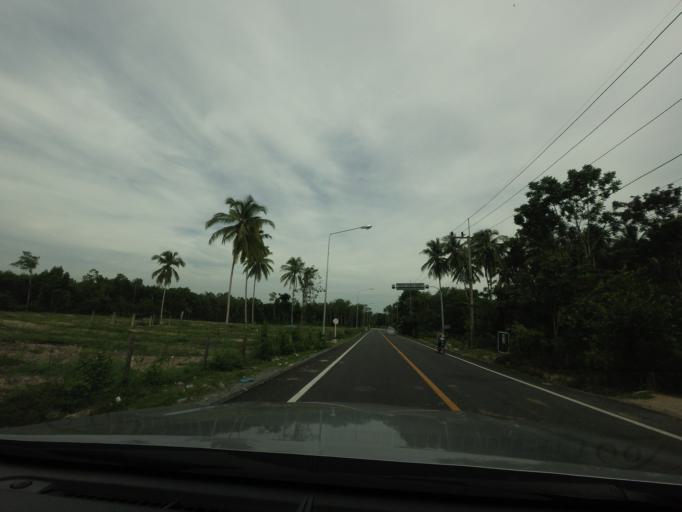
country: TH
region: Yala
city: Raman
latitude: 6.4421
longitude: 101.4522
